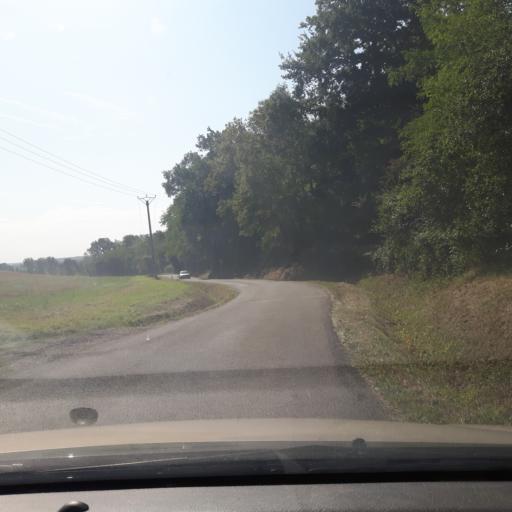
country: FR
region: Midi-Pyrenees
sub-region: Departement de la Haute-Garonne
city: Bouloc
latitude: 43.7708
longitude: 1.4103
